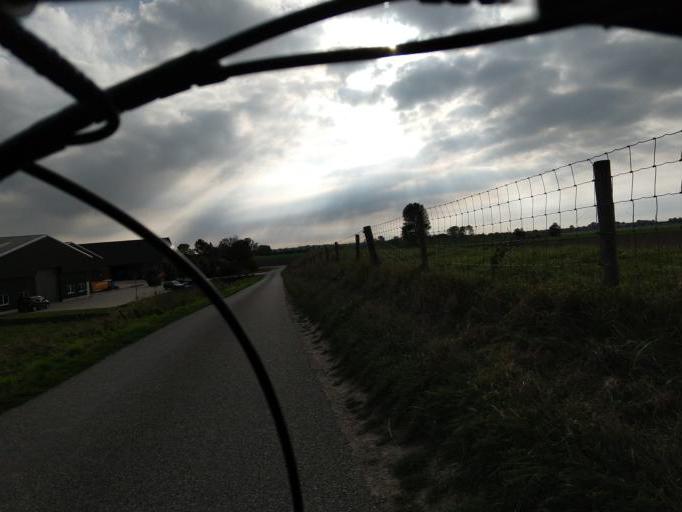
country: NL
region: South Holland
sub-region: Gemeente Goeree-Overflakkee
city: Ouddorp
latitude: 51.7067
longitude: 3.9682
